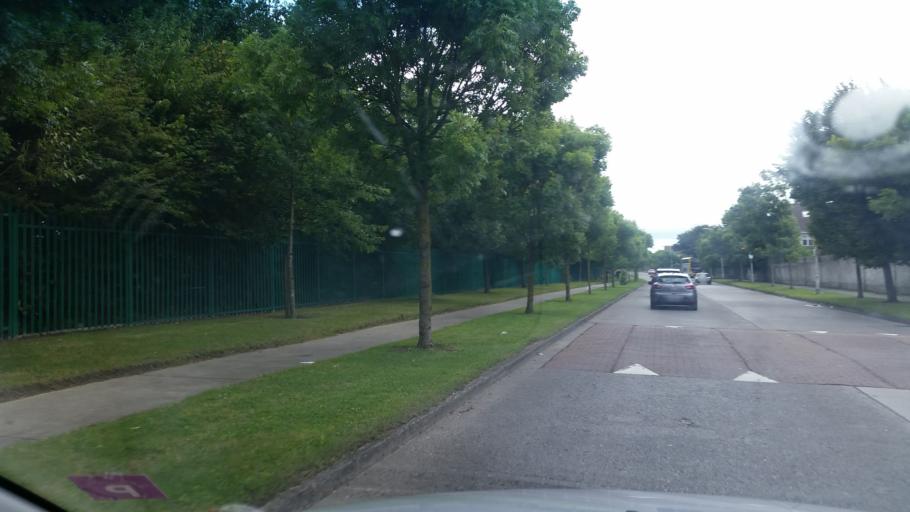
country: IE
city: Darndale
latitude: 53.3970
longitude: -6.1851
